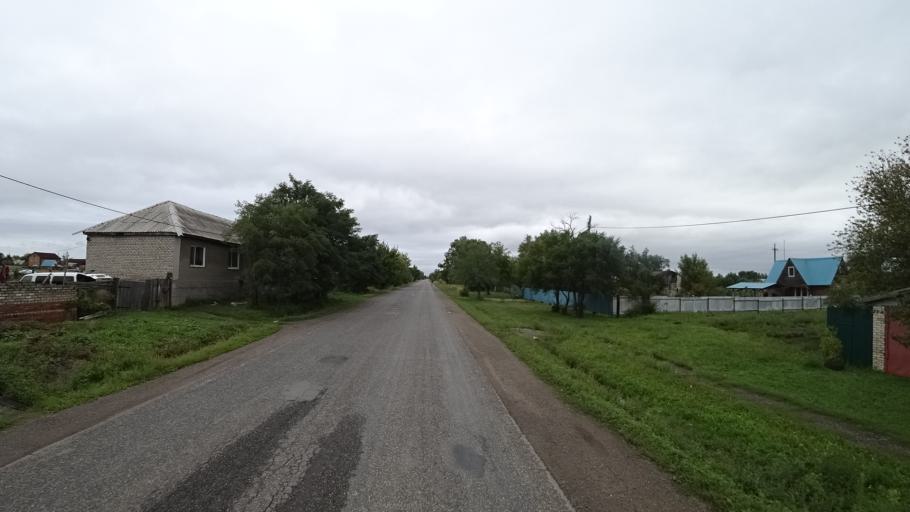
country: RU
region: Primorskiy
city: Chernigovka
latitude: 44.3276
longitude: 132.6023
